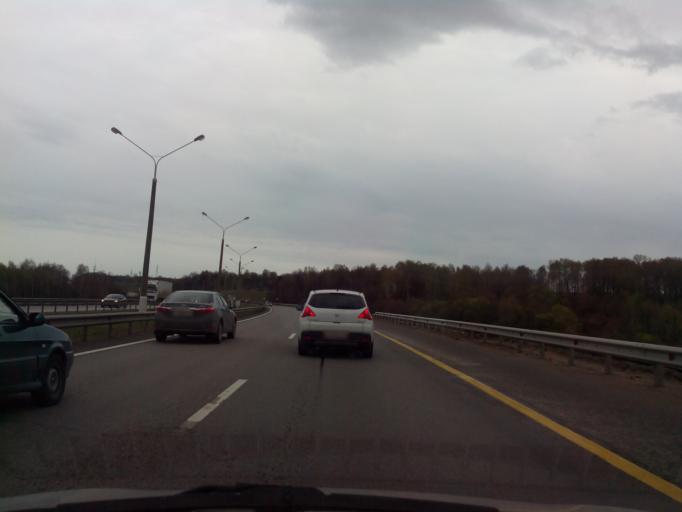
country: RU
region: Moskovskaya
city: Stupino
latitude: 54.8225
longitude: 38.0415
